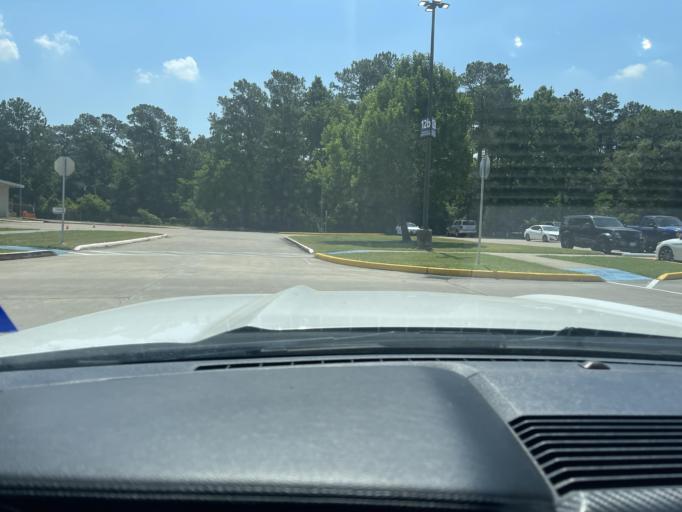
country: US
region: Texas
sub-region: Harris County
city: Cloverleaf
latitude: 29.8111
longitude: -95.1796
